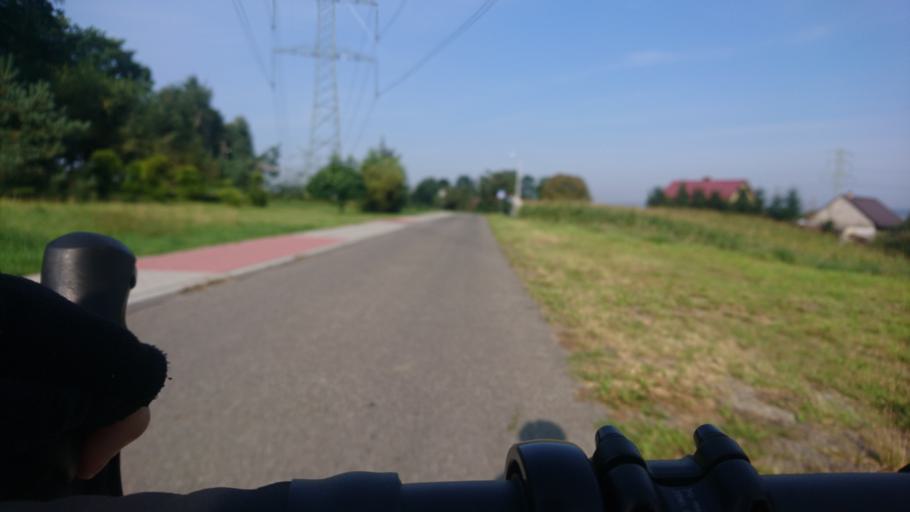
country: PL
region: Lesser Poland Voivodeship
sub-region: Powiat wadowicki
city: Sosnowice
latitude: 49.9502
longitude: 19.7075
